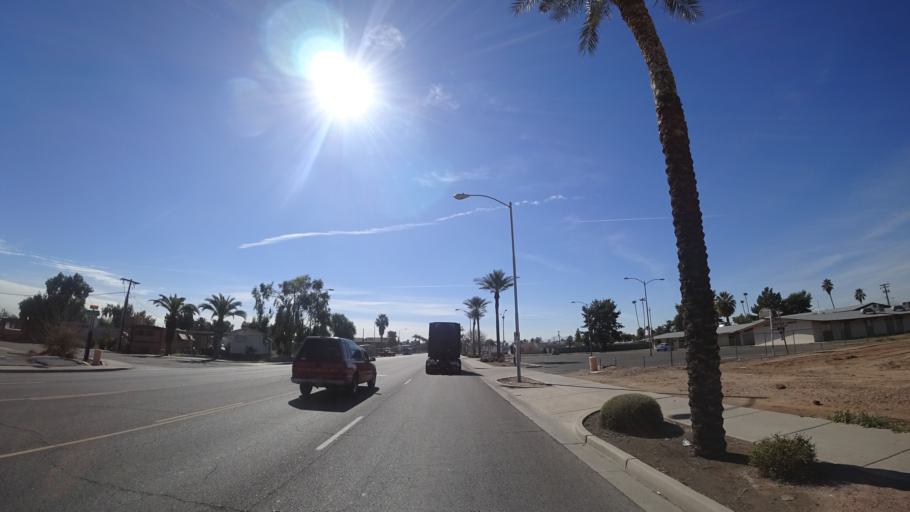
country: US
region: Arizona
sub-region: Maricopa County
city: Glendale
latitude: 33.5295
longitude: -112.1864
